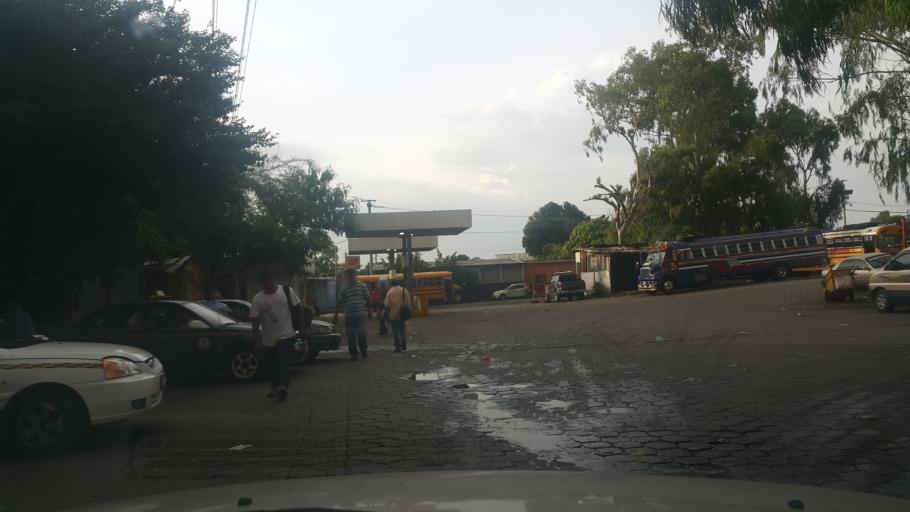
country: NI
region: Managua
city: Managua
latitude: 12.1285
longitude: -86.3009
